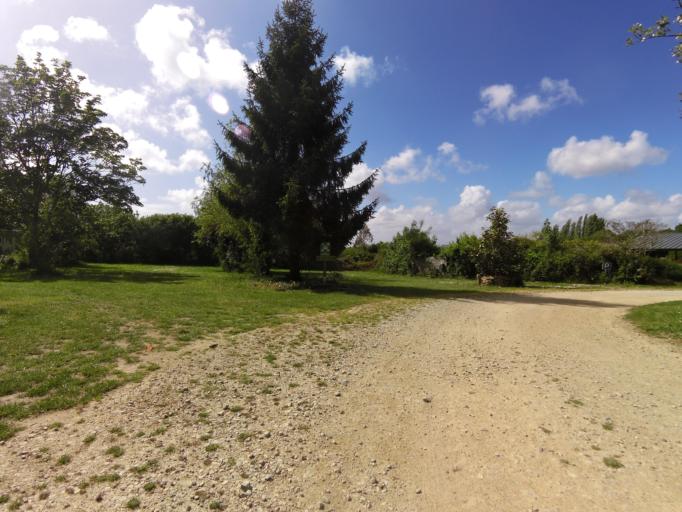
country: FR
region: Brittany
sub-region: Departement du Morbihan
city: Plougoumelen
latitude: 47.6433
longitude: -2.8991
